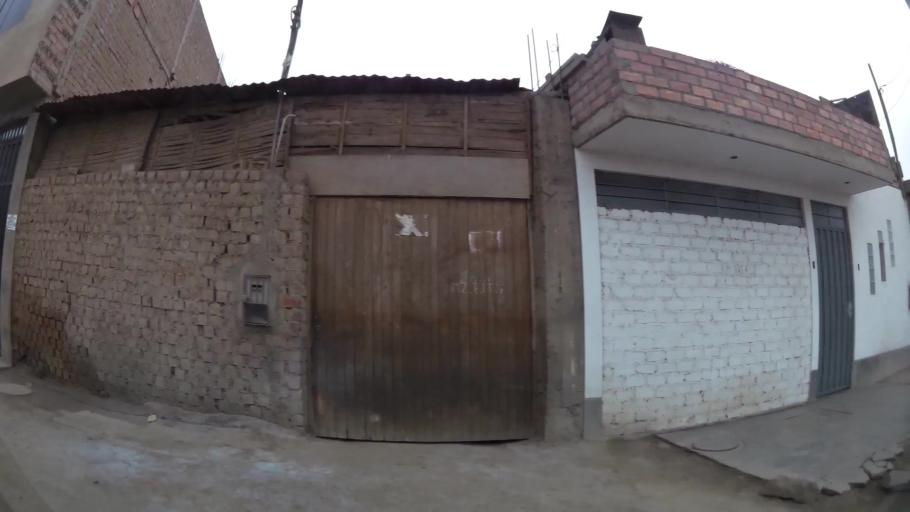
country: PE
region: Lima
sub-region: Lima
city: Urb. Santo Domingo
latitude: -11.8642
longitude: -77.0168
